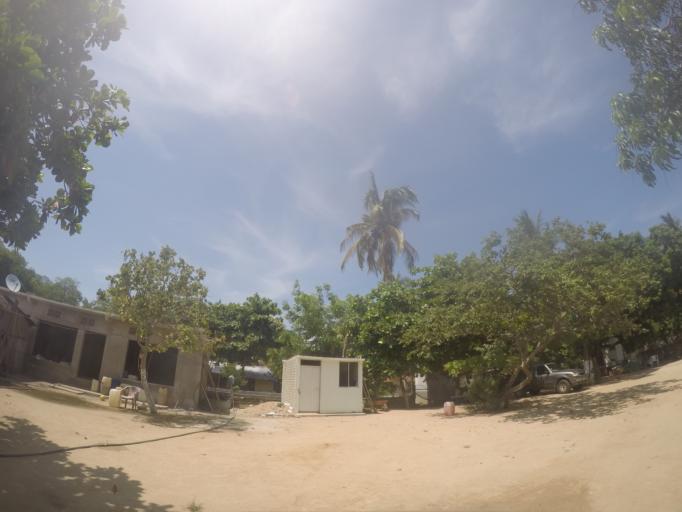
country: MX
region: Oaxaca
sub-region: Villa de Tututepec de Melchor Ocampo
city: Santa Rosa de Lima
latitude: 15.9885
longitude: -97.5495
